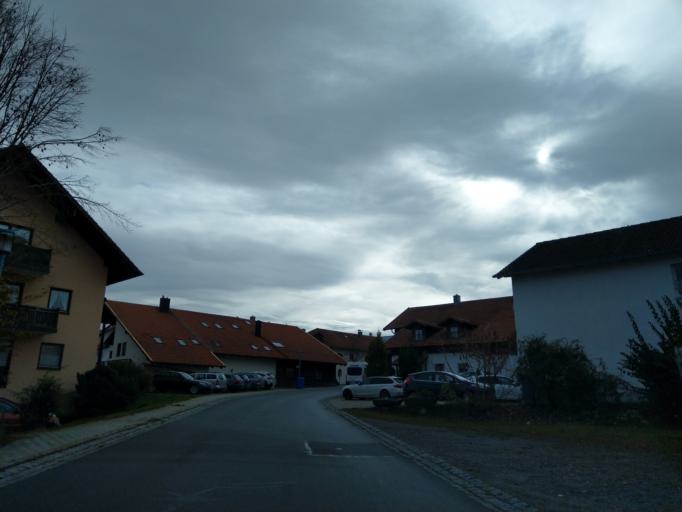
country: DE
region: Bavaria
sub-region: Lower Bavaria
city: Schofweg
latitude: 48.8405
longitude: 13.2282
